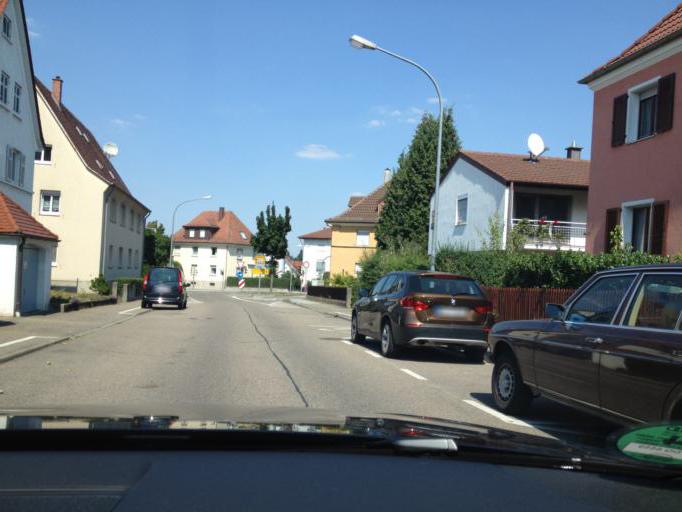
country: DE
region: Baden-Wuerttemberg
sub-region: Regierungsbezirk Stuttgart
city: Neckarsulm
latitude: 49.1875
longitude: 9.2307
